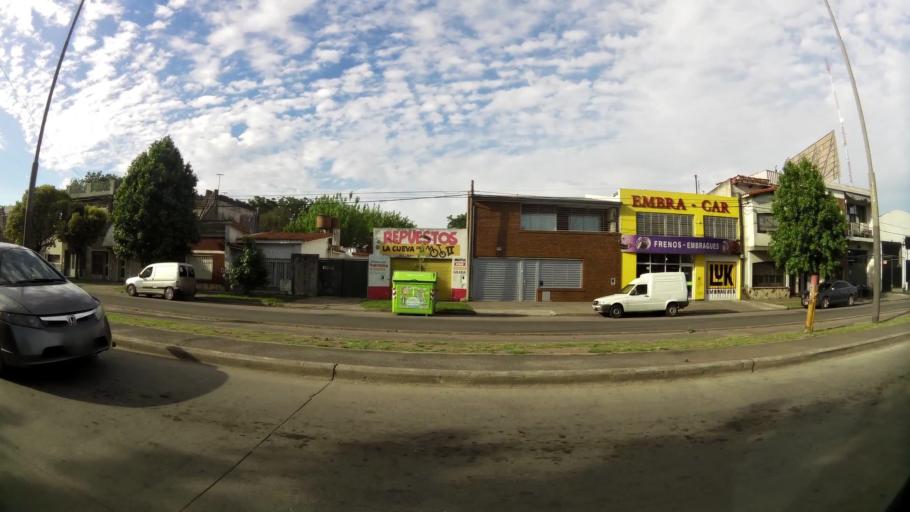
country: AR
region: Santa Fe
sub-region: Departamento de Rosario
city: Rosario
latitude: -32.9749
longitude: -60.6702
